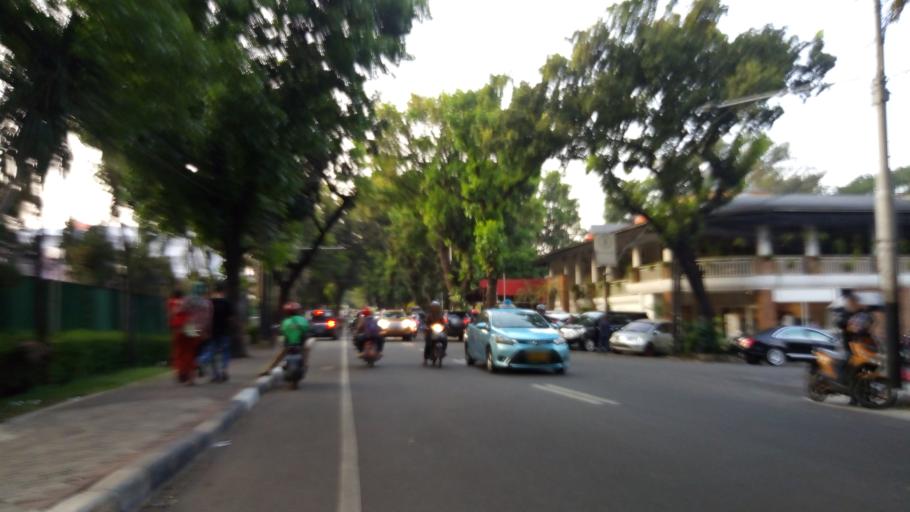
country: ID
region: Jakarta Raya
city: Jakarta
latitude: -6.2456
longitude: 106.7916
